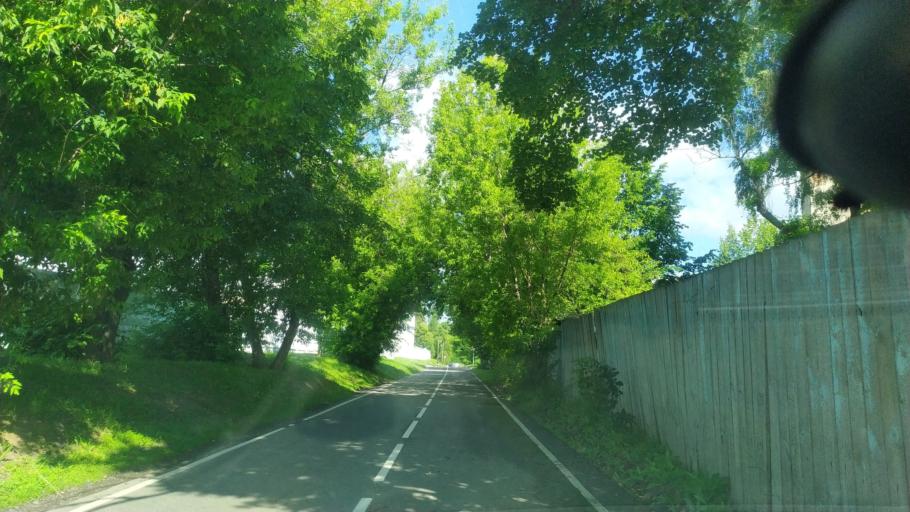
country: RU
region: Moscow
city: Vostochnyy
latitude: 55.8152
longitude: 37.8625
